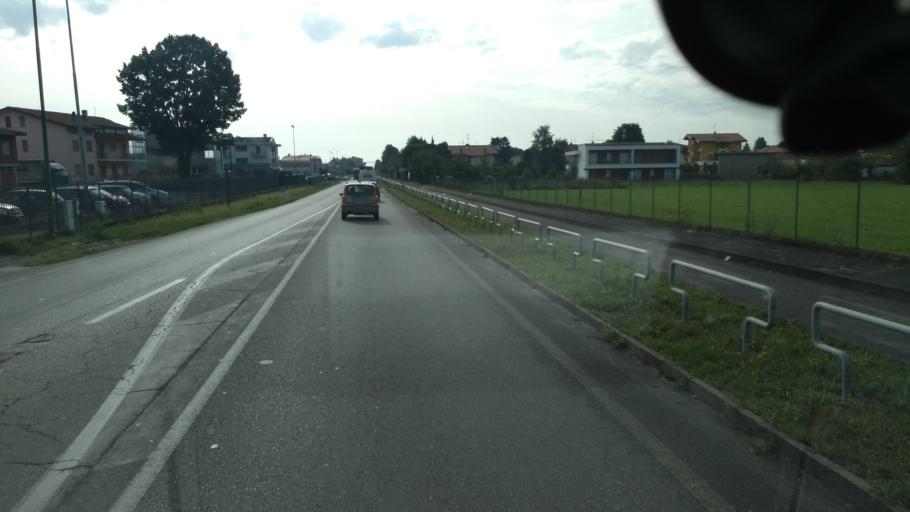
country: IT
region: Lombardy
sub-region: Provincia di Bergamo
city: Urgnano
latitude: 45.6073
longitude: 9.6963
